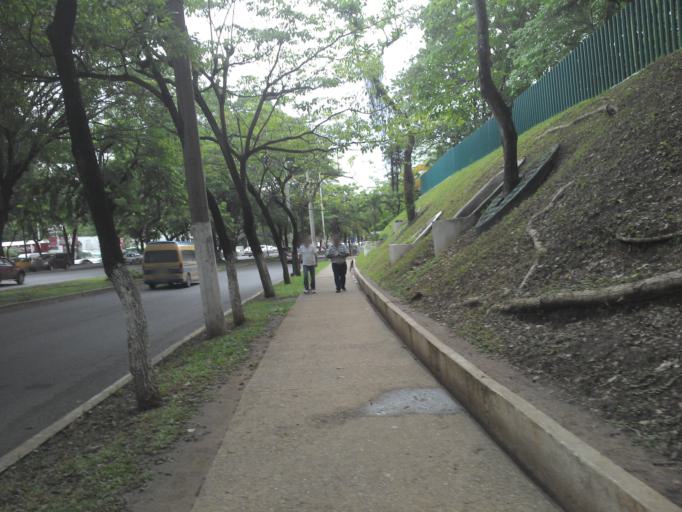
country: MX
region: Tabasco
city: Villahermosa
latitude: 18.0017
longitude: -92.9350
